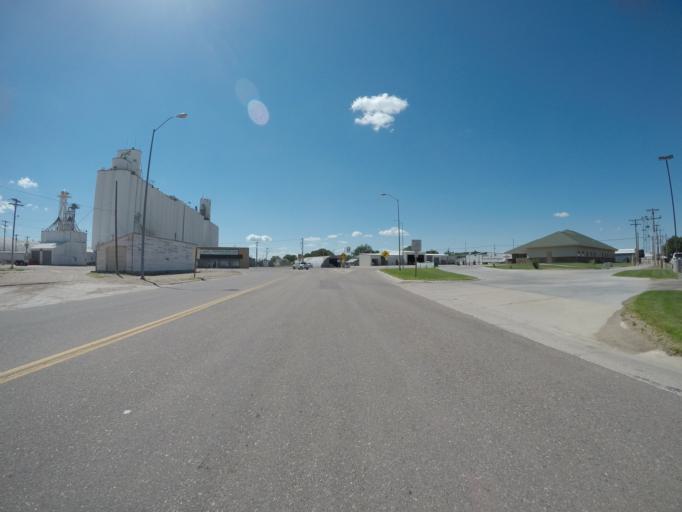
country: US
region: Nebraska
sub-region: Chase County
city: Imperial
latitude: 40.5125
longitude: -101.6422
